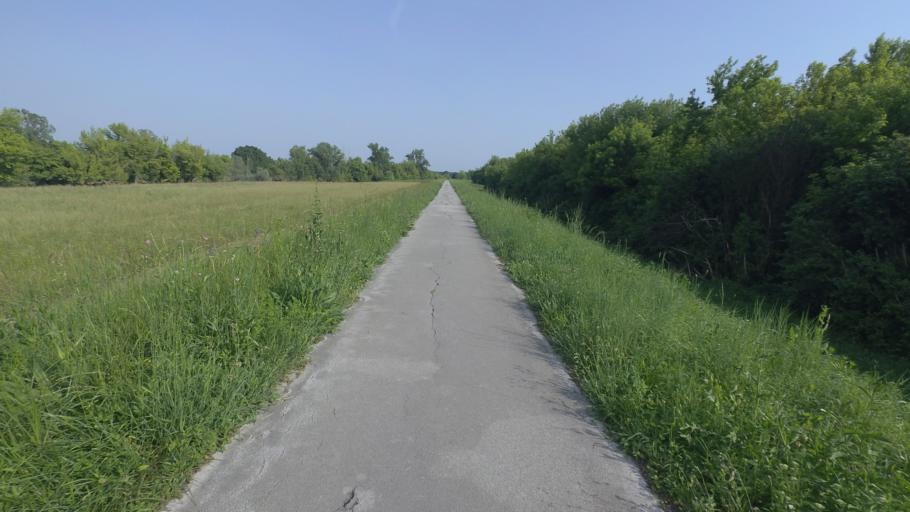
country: HR
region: Karlovacka
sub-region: Grad Karlovac
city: Karlovac
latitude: 45.4951
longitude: 15.5694
